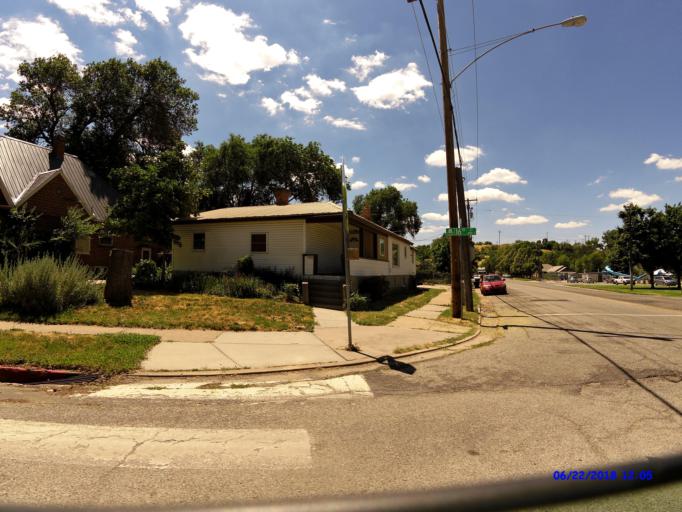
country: US
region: Utah
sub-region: Weber County
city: Ogden
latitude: 41.2379
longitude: -111.9577
